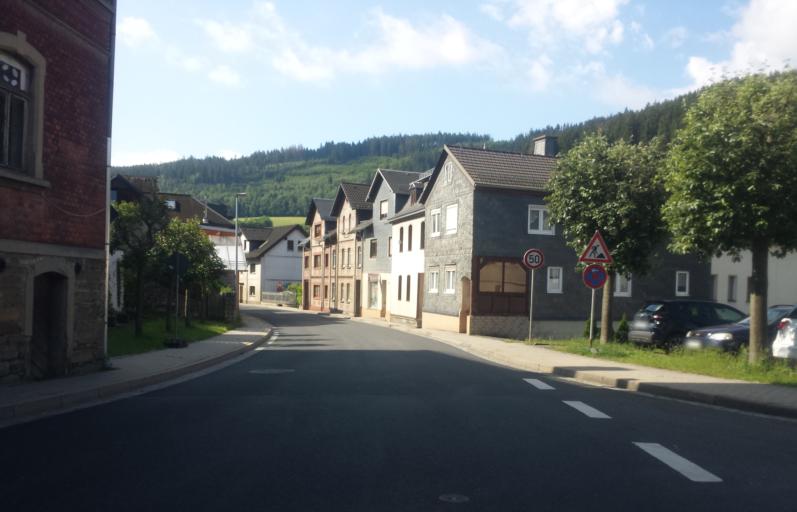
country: DE
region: Thuringia
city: Probstzella
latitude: 50.5316
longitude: 11.3801
